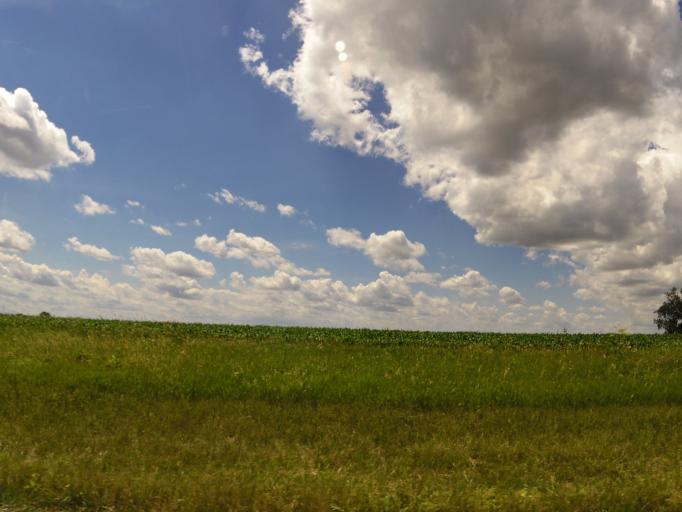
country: US
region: Iowa
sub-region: Buchanan County
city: Independence
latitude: 42.5334
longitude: -91.8900
